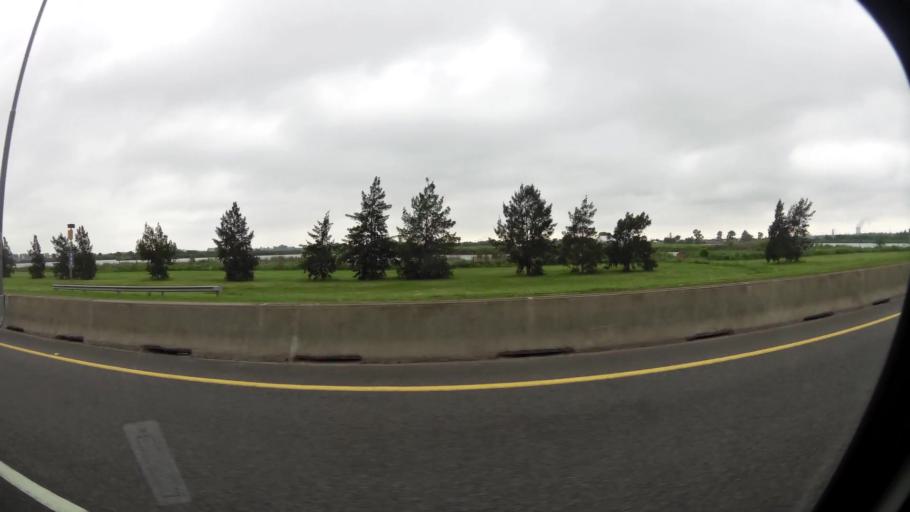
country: AR
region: Buenos Aires
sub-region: Partido de La Plata
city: La Plata
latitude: -34.8804
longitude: -57.9634
